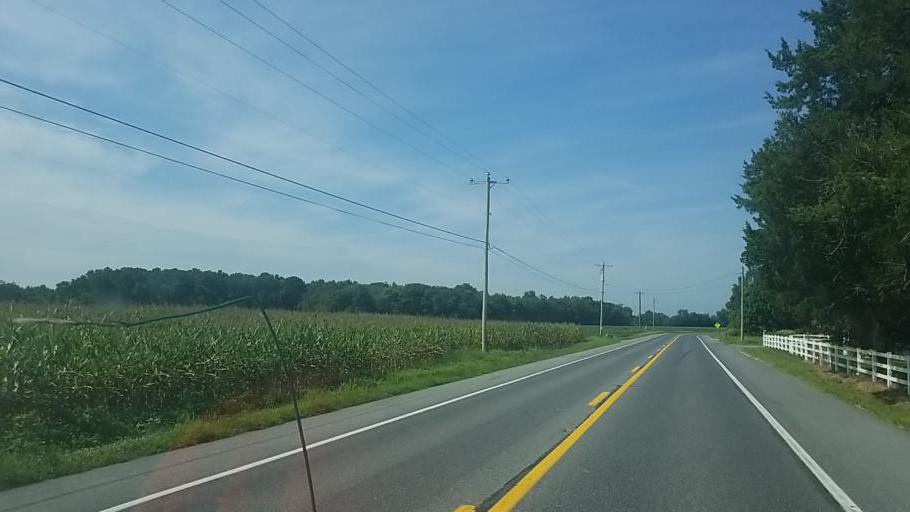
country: US
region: Delaware
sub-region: Sussex County
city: Millsboro
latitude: 38.5393
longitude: -75.2628
